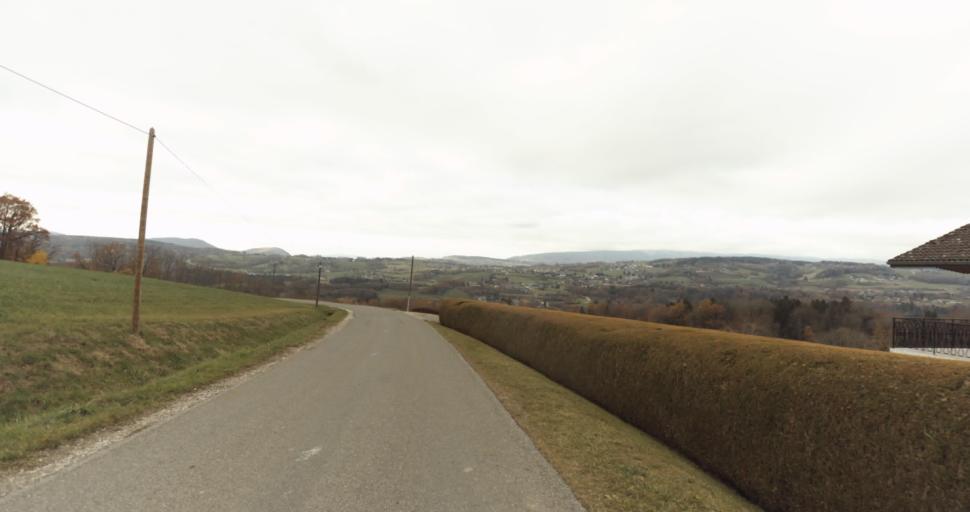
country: FR
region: Rhone-Alpes
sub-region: Departement de la Haute-Savoie
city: Groisy
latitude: 45.9946
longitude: 6.1938
